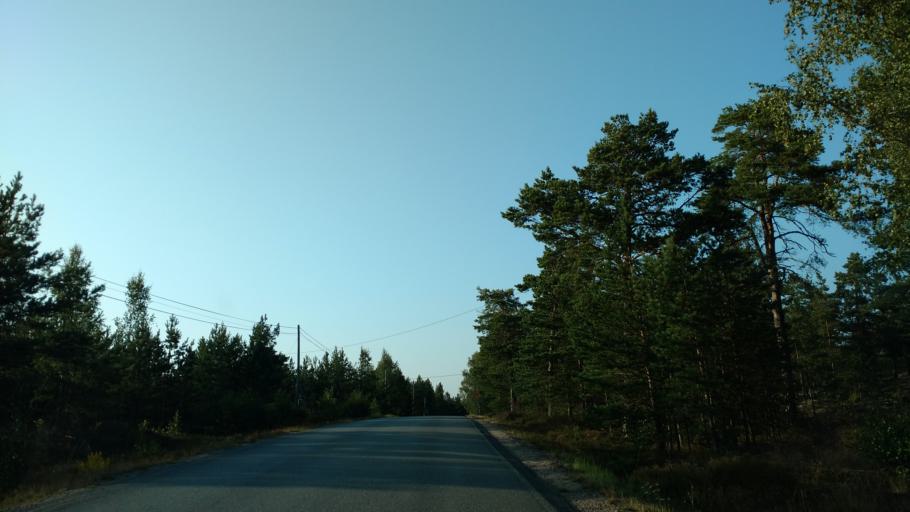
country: FI
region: Varsinais-Suomi
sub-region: Aboland-Turunmaa
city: Dragsfjaerd
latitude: 59.9447
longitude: 22.4143
